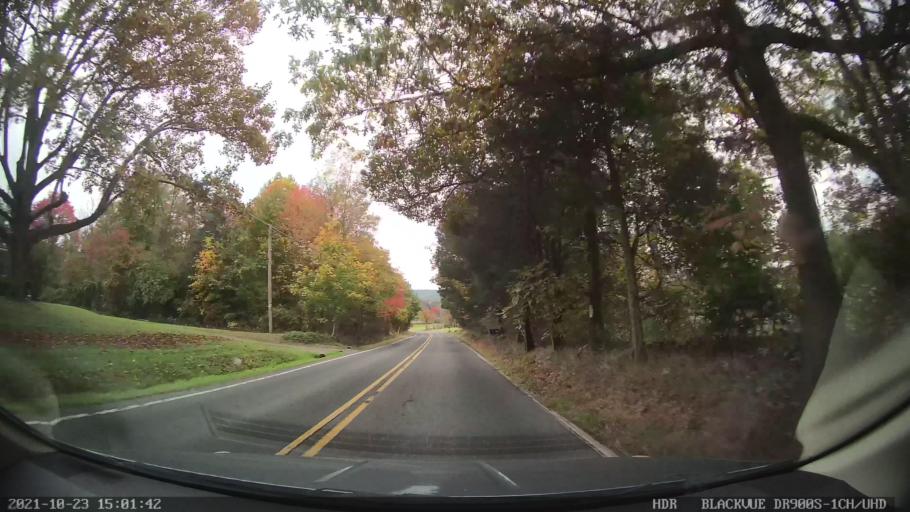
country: US
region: Pennsylvania
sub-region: Berks County
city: Bally
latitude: 40.4060
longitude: -75.5503
